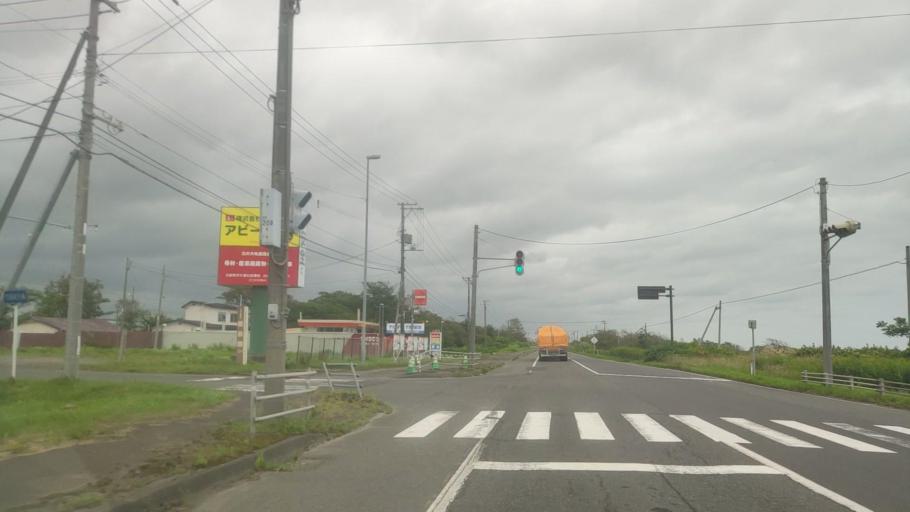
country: JP
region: Hokkaido
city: Shiraoi
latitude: 42.4955
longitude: 141.2657
